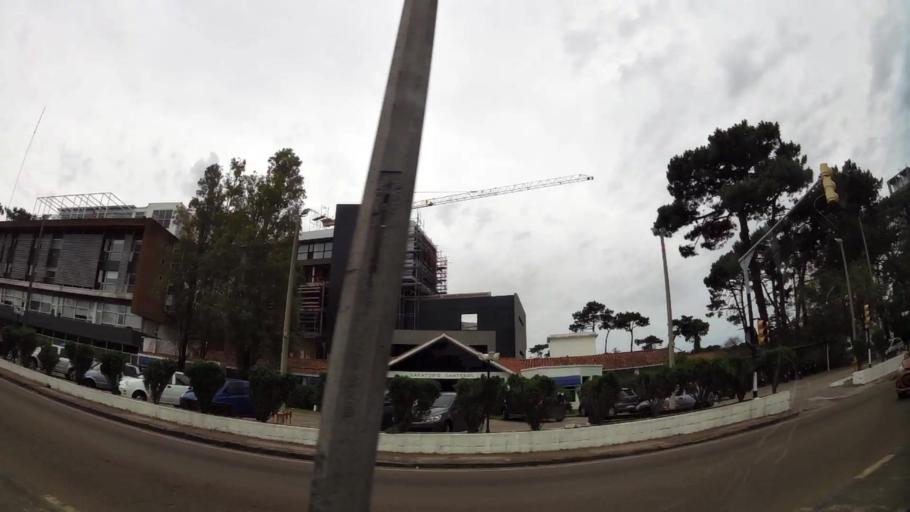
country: UY
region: Maldonado
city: Maldonado
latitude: -34.9306
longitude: -54.9437
